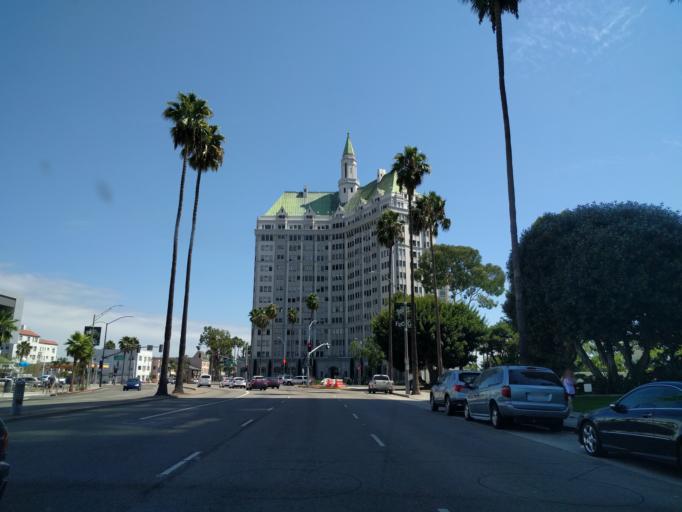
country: US
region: California
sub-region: Los Angeles County
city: Long Beach
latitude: 33.7662
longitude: -118.1844
